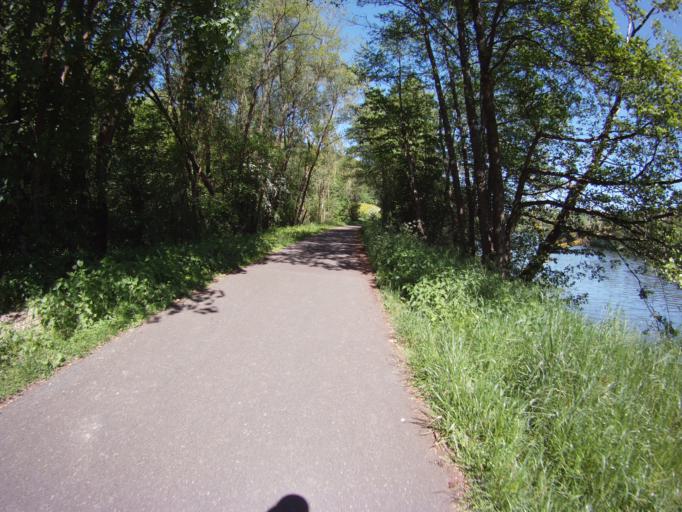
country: FR
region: Lorraine
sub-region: Departement de Meurthe-et-Moselle
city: Chaligny
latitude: 48.6363
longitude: 6.0408
